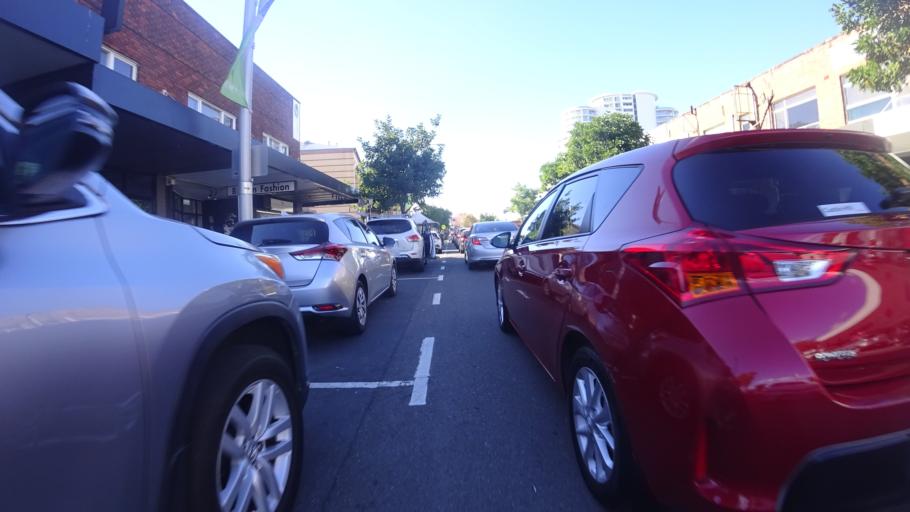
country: AU
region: New South Wales
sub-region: The Hills Shire
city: Castle Hill
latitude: -33.7330
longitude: 151.0047
